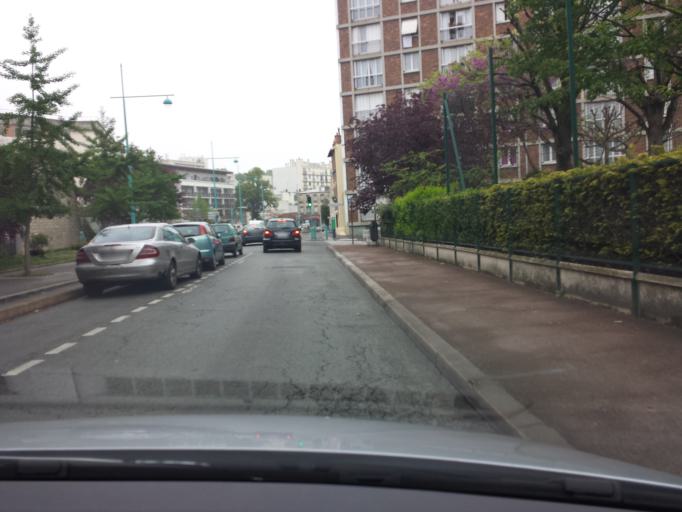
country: FR
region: Ile-de-France
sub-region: Departement du Val-de-Marne
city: Gentilly
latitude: 48.8125
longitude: 2.3466
